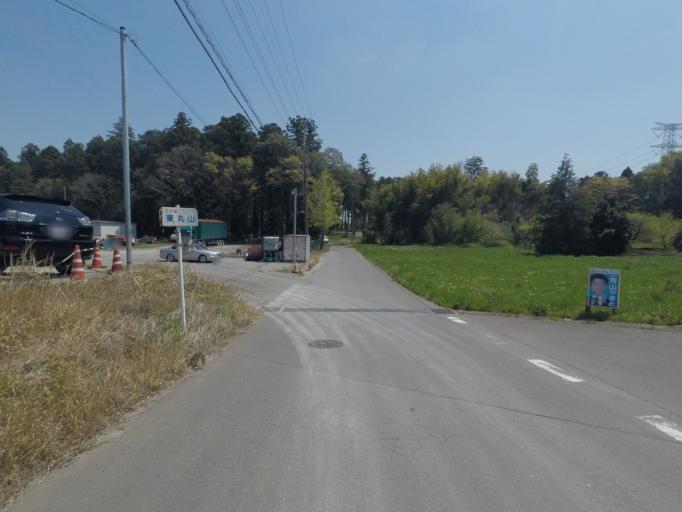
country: JP
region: Ibaraki
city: Ushiku
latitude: 36.0163
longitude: 140.0898
